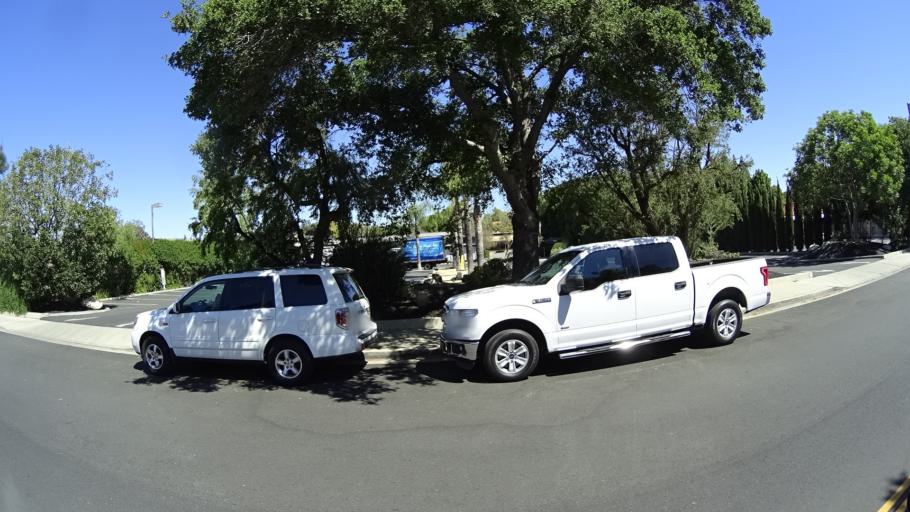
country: US
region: California
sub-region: Ventura County
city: Thousand Oaks
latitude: 34.1778
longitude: -118.8705
